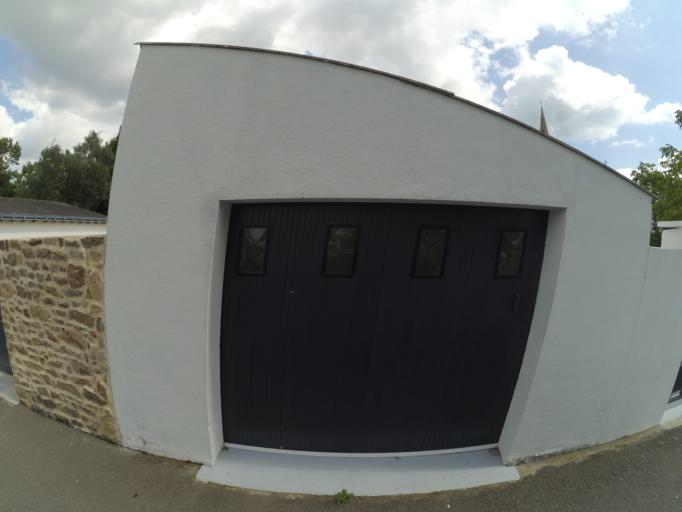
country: FR
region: Brittany
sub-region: Departement du Morbihan
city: Auray
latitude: 47.6792
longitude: -3.0003
